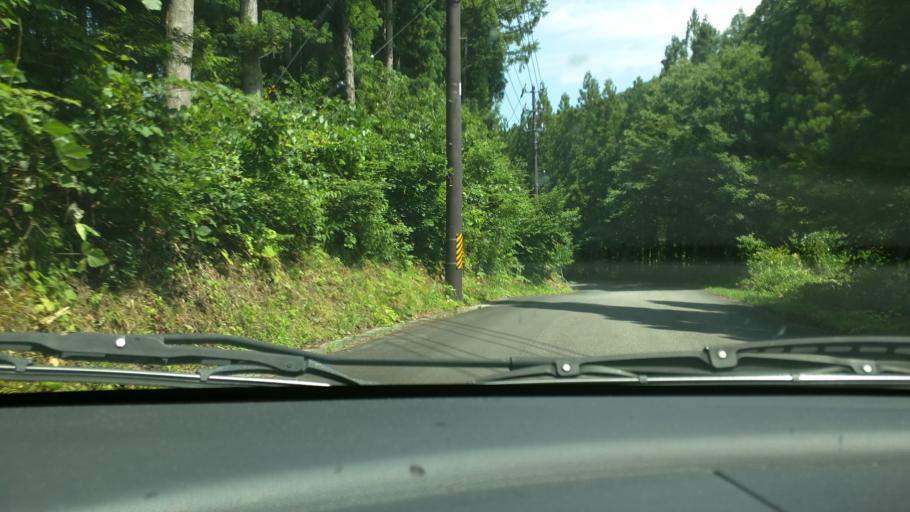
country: JP
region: Fukushima
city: Inawashiro
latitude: 37.3587
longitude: 140.0570
